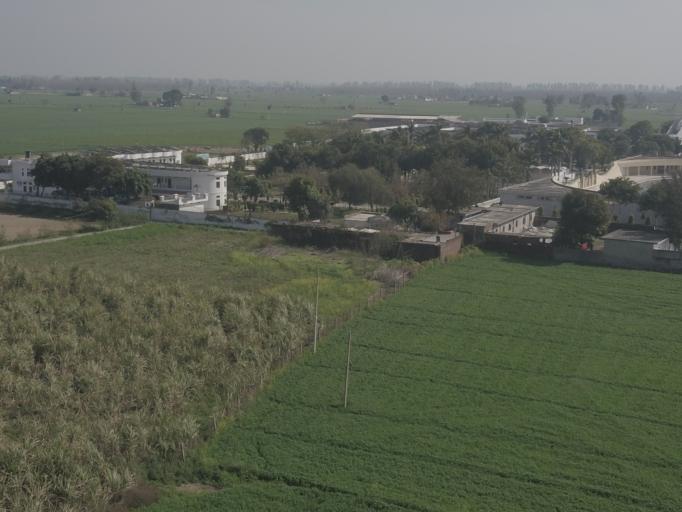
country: IN
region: Punjab
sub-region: Shahid Bhagat Singh Nagar
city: Rahon
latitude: 31.0231
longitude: 76.0907
